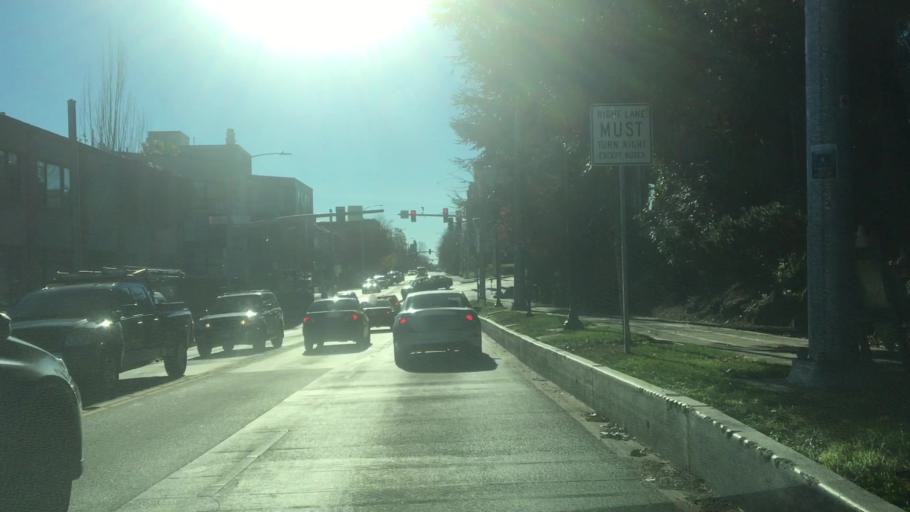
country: US
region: Washington
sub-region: King County
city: Seattle
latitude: 47.6199
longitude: -122.3026
